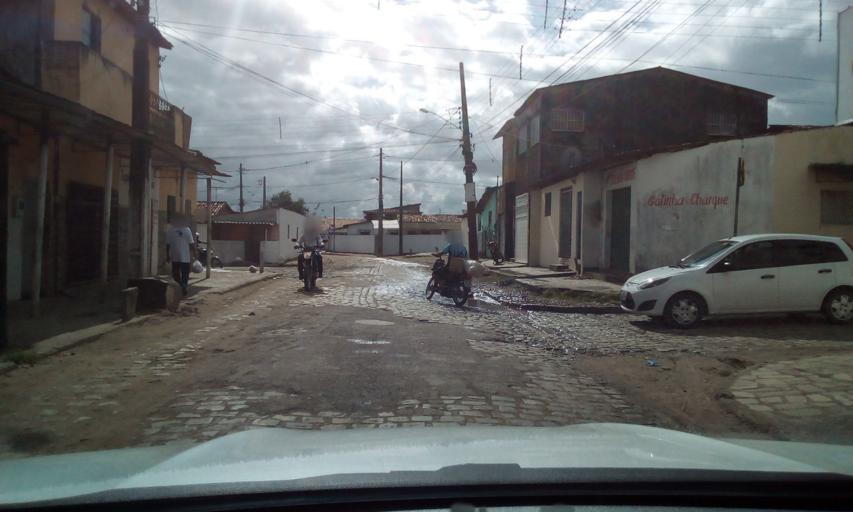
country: BR
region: Paraiba
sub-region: Joao Pessoa
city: Joao Pessoa
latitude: -7.1877
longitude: -34.8838
